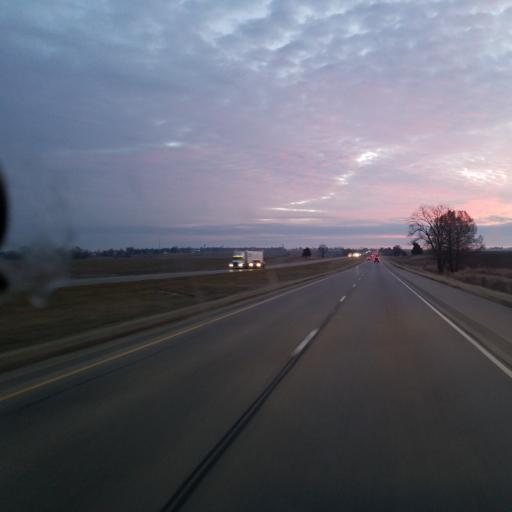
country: US
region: Illinois
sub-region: Tazewell County
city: Mackinaw
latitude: 40.6223
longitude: -89.3641
